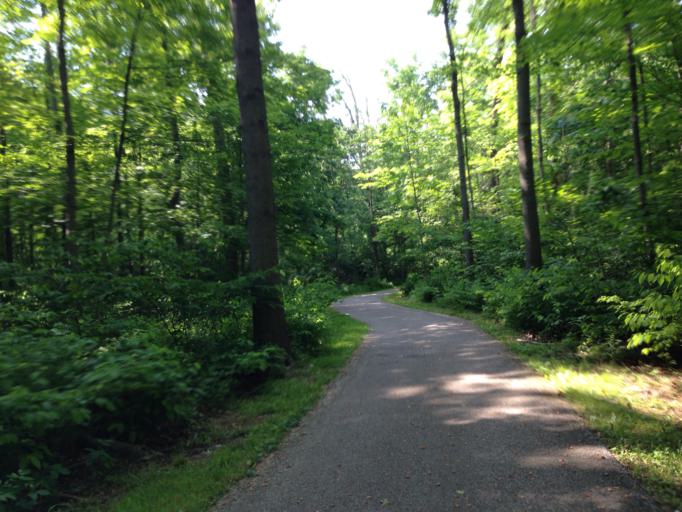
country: US
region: Ohio
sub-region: Cuyahoga County
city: Olmsted Falls
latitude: 41.3928
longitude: -81.8791
